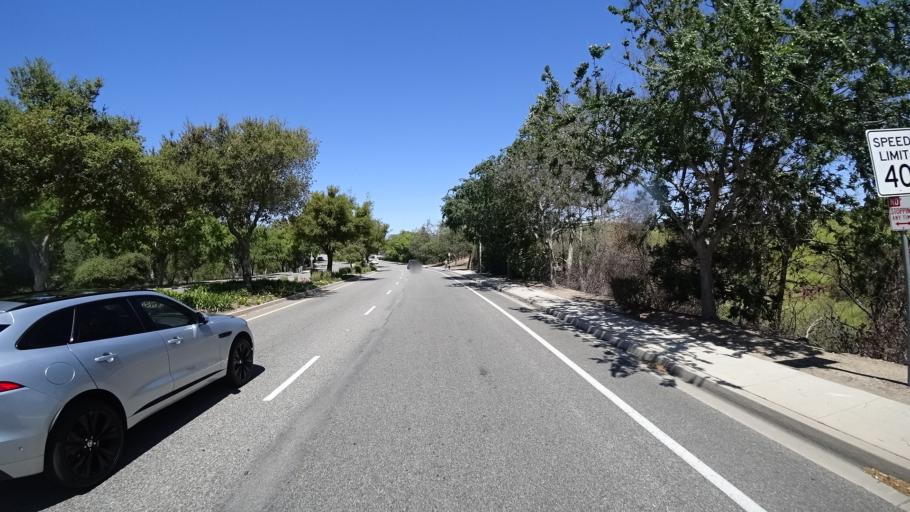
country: US
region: California
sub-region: Ventura County
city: Casa Conejo
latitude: 34.1893
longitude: -118.9113
